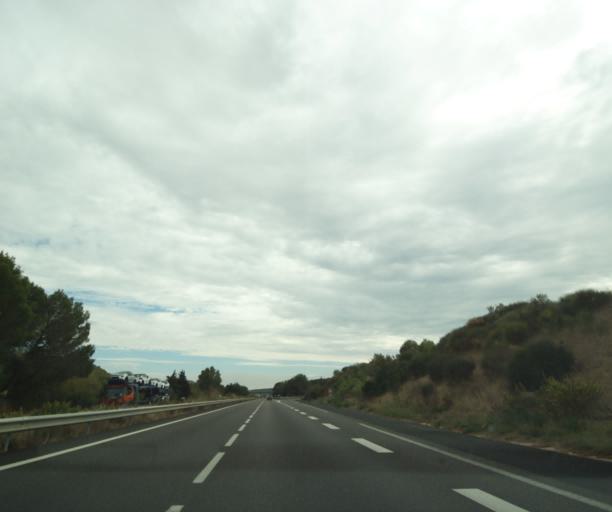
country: FR
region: Languedoc-Roussillon
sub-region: Departement du Gard
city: Garons
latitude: 43.7618
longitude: 4.4246
